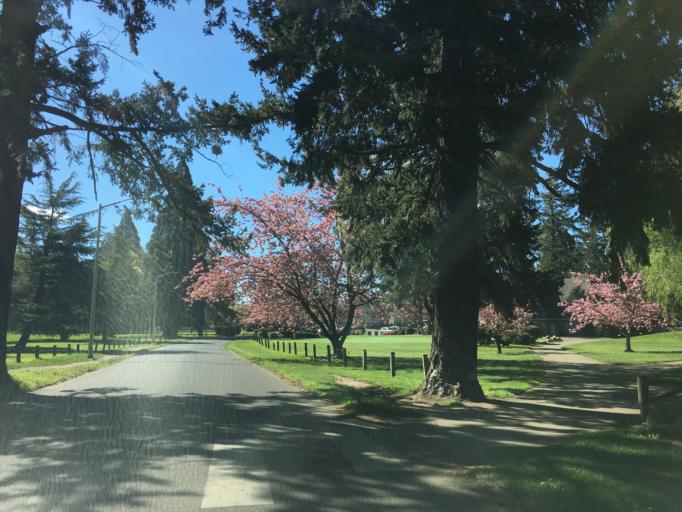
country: US
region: Oregon
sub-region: Multnomah County
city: Lents
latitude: 45.5391
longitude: -122.5898
